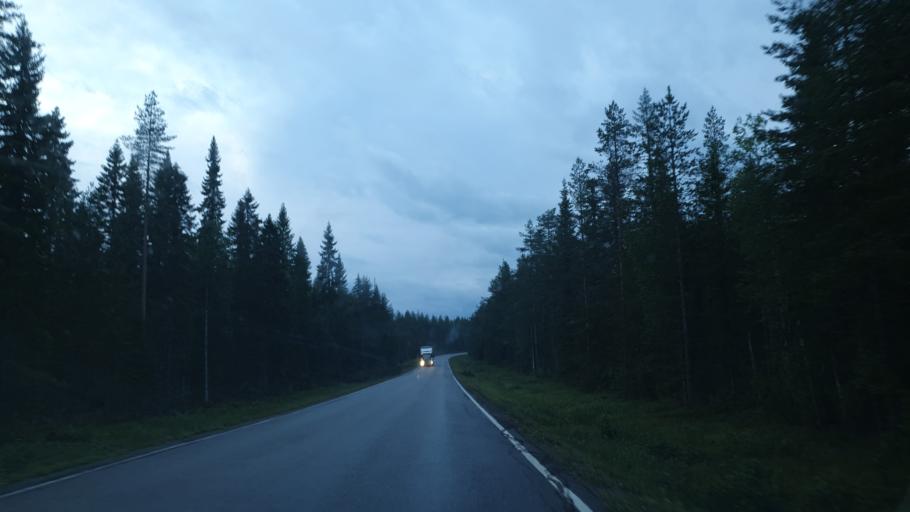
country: FI
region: Kainuu
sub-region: Kehys-Kainuu
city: Kuhmo
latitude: 63.9577
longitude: 29.7059
